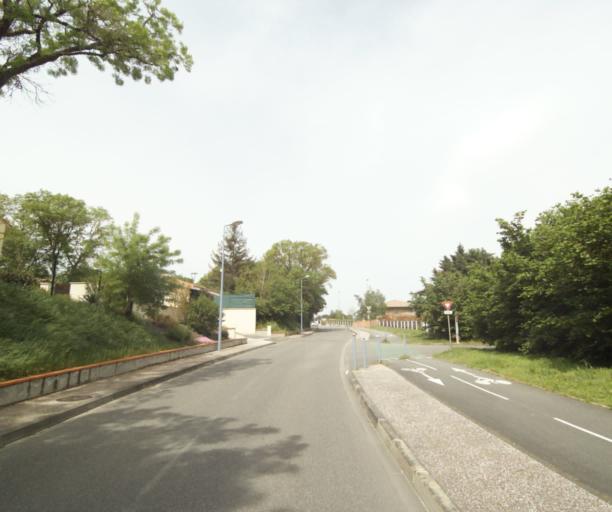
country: FR
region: Midi-Pyrenees
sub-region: Departement de la Haute-Garonne
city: Auzeville-Tolosane
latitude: 43.5222
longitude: 1.4904
